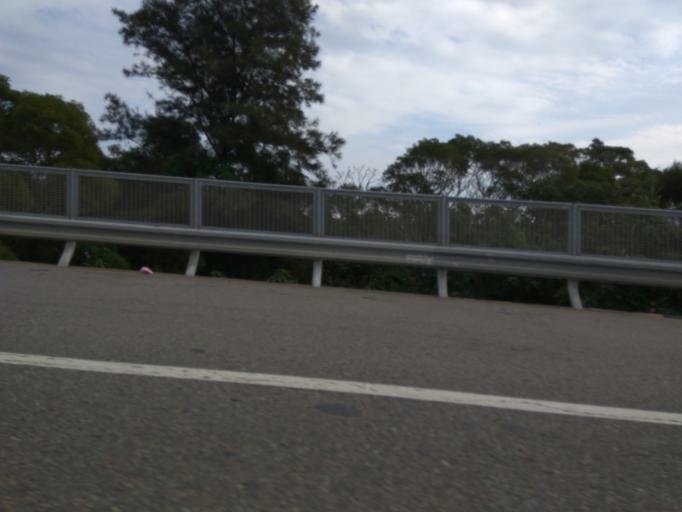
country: TW
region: Taiwan
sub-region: Hsinchu
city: Zhubei
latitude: 24.9414
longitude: 121.0027
